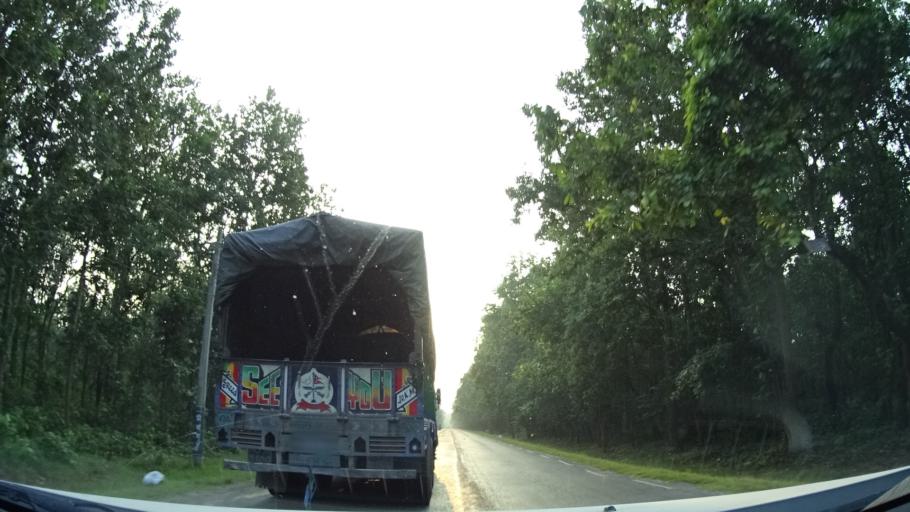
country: NP
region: Central Region
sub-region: Narayani Zone
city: Bharatpur
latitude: 27.6260
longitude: 84.0573
